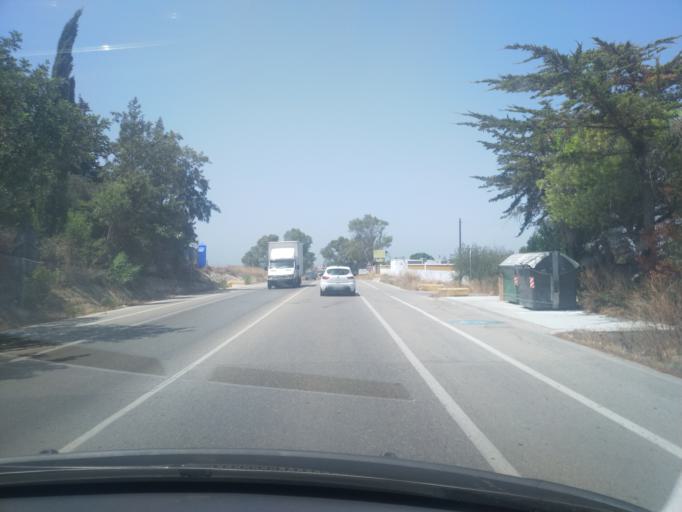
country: ES
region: Andalusia
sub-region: Provincia de Cadiz
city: Chiclana de la Frontera
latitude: 36.3920
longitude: -6.1435
